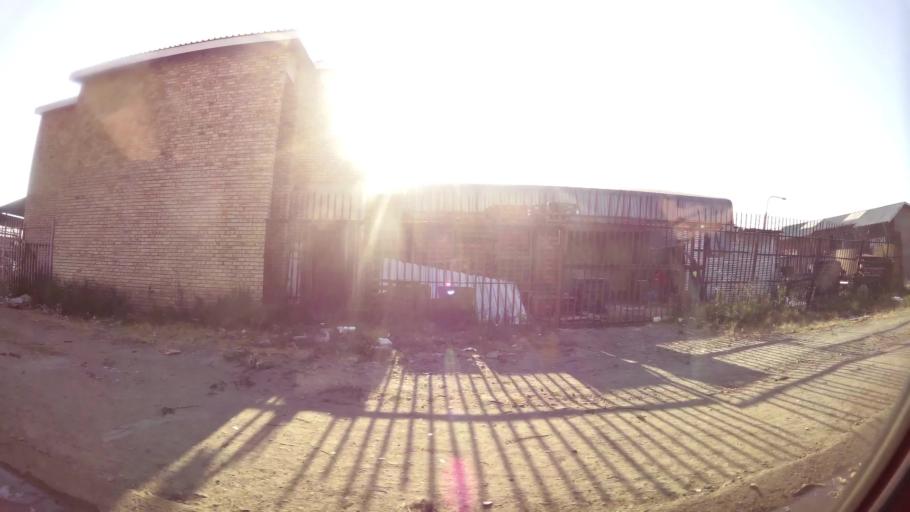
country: ZA
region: North-West
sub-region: Bojanala Platinum District Municipality
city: Rustenburg
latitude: -25.6500
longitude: 27.2415
